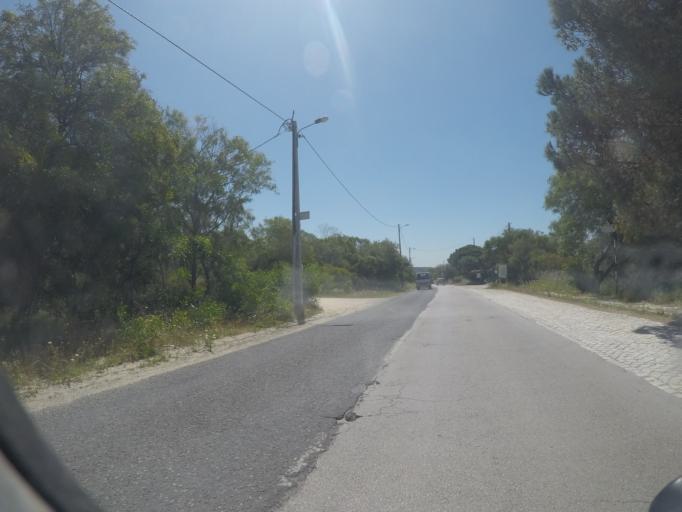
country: PT
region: Setubal
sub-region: Almada
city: Charneca
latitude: 38.6179
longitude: -9.2125
